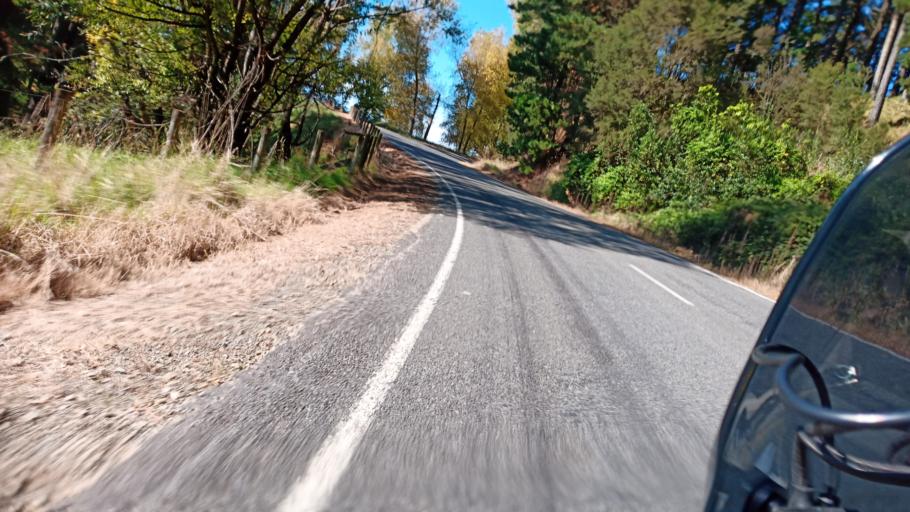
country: NZ
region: Hawke's Bay
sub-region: Wairoa District
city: Wairoa
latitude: -38.9245
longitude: 177.2410
